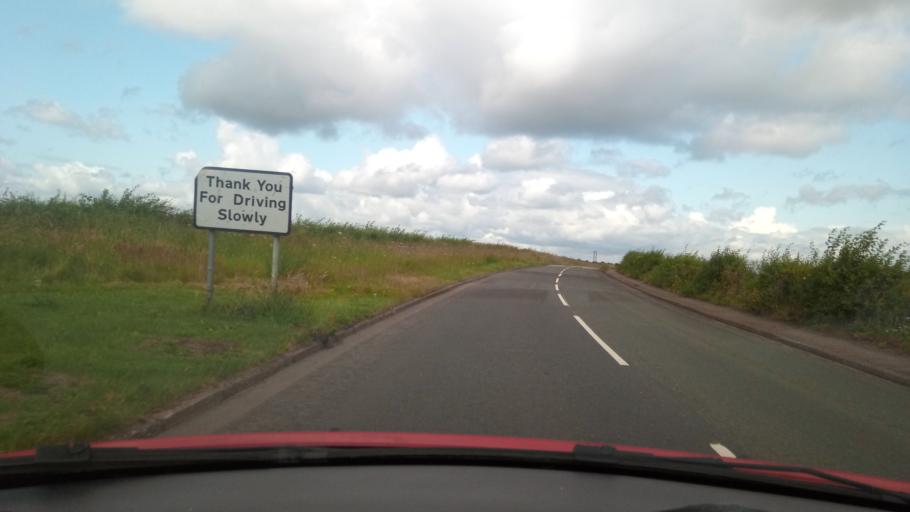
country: GB
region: Scotland
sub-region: East Lothian
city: Macmerry
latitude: 55.9310
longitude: -2.9247
